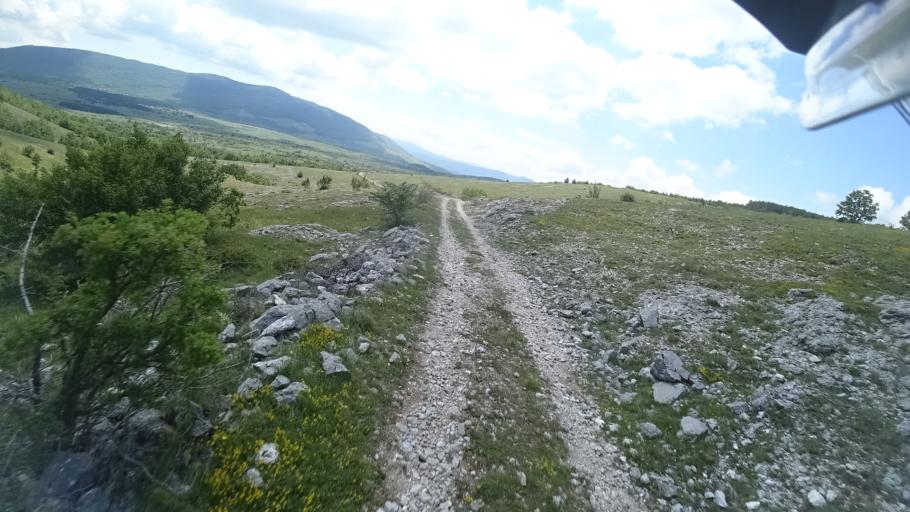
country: HR
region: Zadarska
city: Gracac
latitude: 44.3695
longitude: 15.9557
